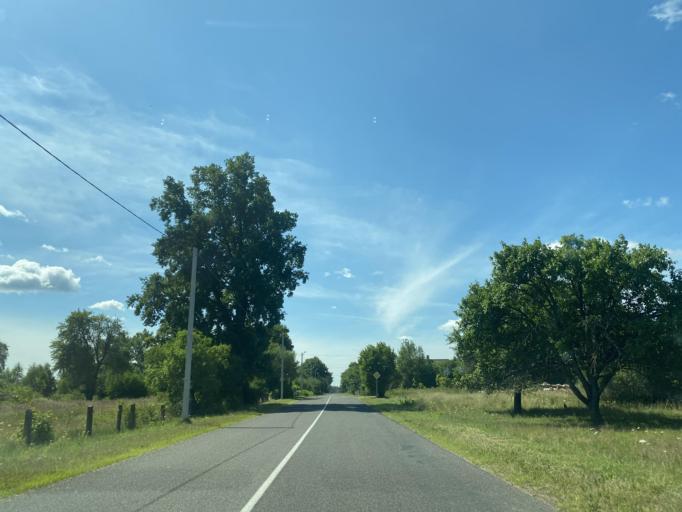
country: BY
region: Brest
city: Ivanava
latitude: 52.2032
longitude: 25.6153
